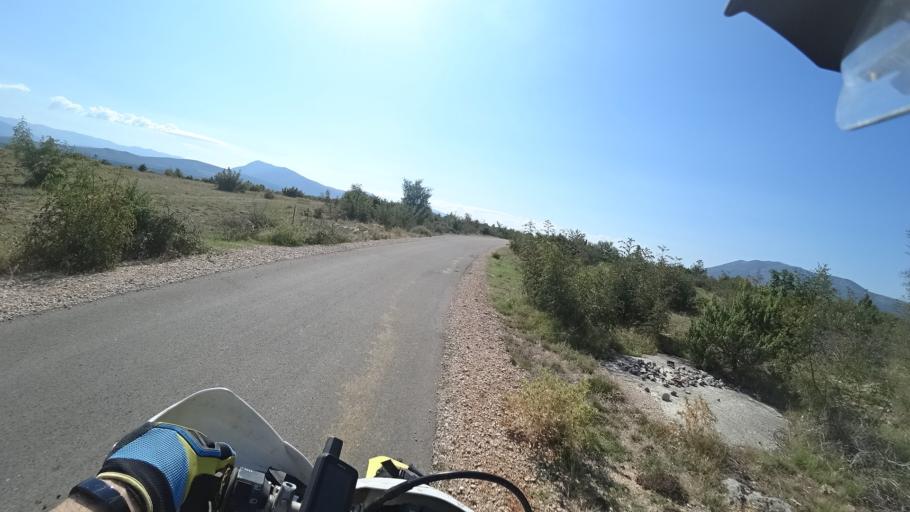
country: HR
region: Sibensko-Kniniska
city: Knin
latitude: 44.0072
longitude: 16.1927
